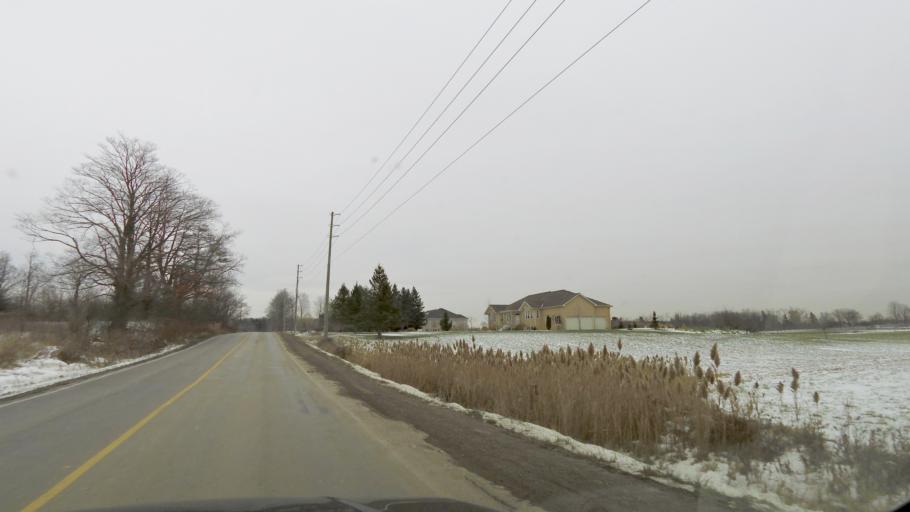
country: CA
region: Ontario
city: Vaughan
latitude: 43.8741
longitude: -79.6031
